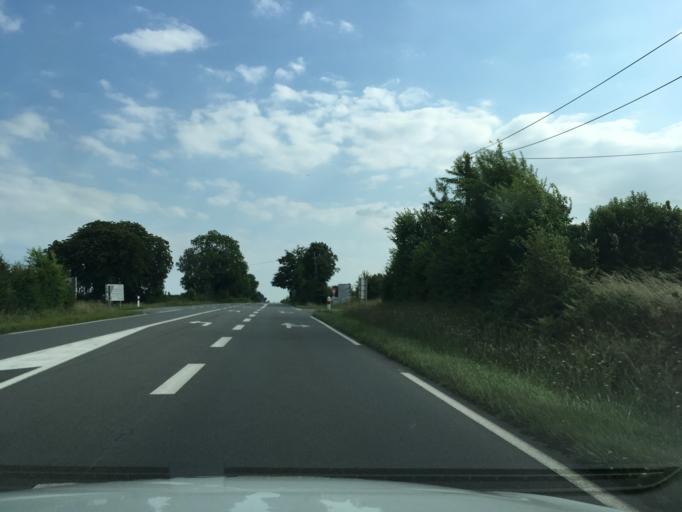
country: FR
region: Poitou-Charentes
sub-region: Departement des Deux-Sevres
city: Le Tallud
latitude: 46.6000
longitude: -0.2885
